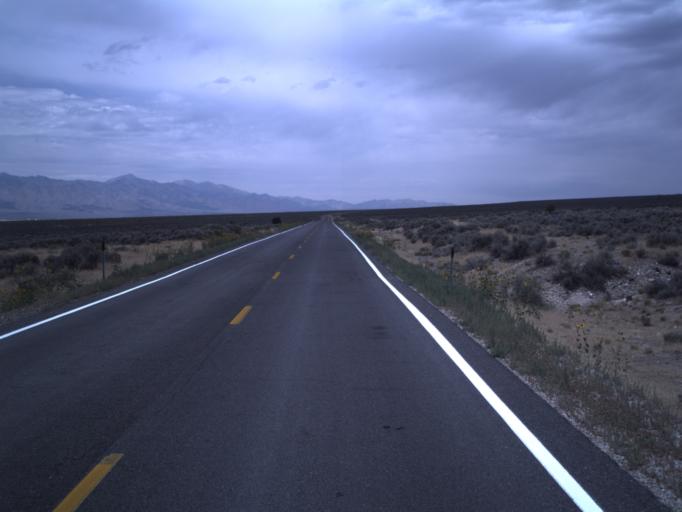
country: US
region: Utah
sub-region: Utah County
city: Eagle Mountain
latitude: 40.2798
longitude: -112.2565
